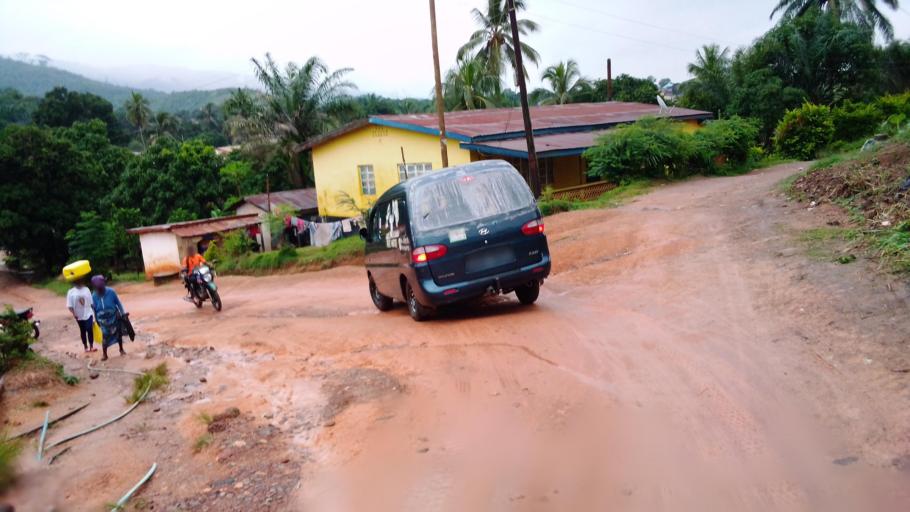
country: SL
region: Eastern Province
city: Kenema
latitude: 7.8923
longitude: -11.1872
